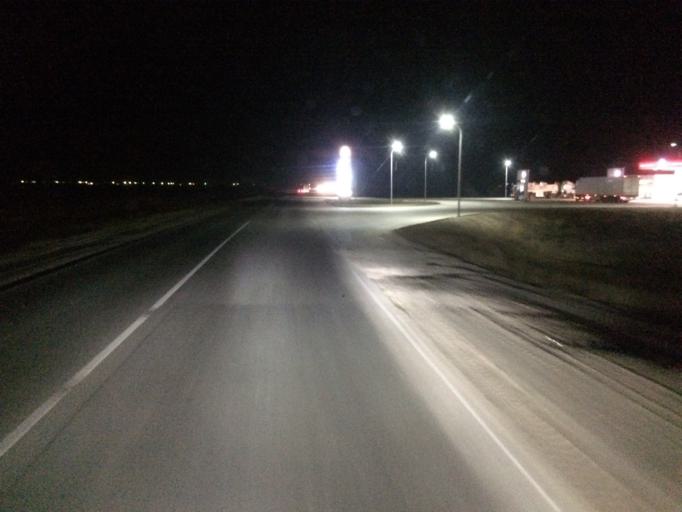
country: KZ
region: Batys Qazaqstan
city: Oral
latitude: 51.2181
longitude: 51.2777
